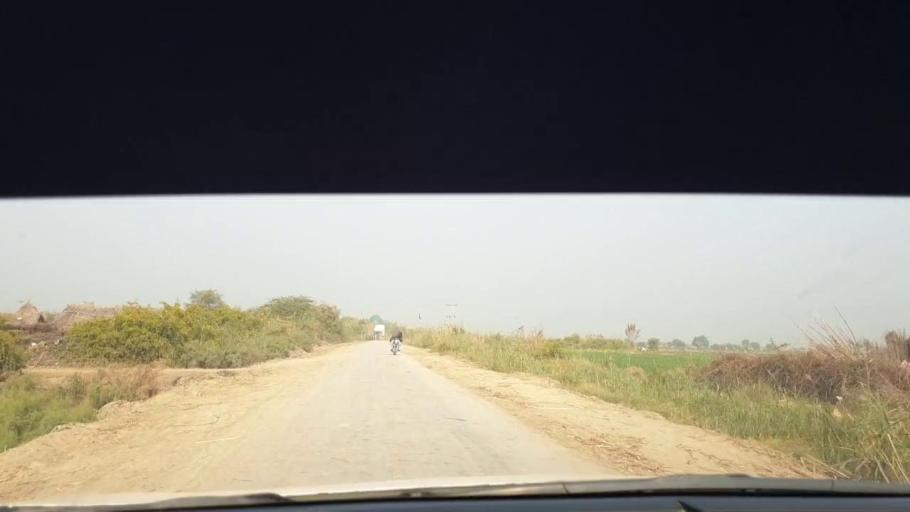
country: PK
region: Sindh
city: Berani
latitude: 25.8003
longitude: 68.8365
